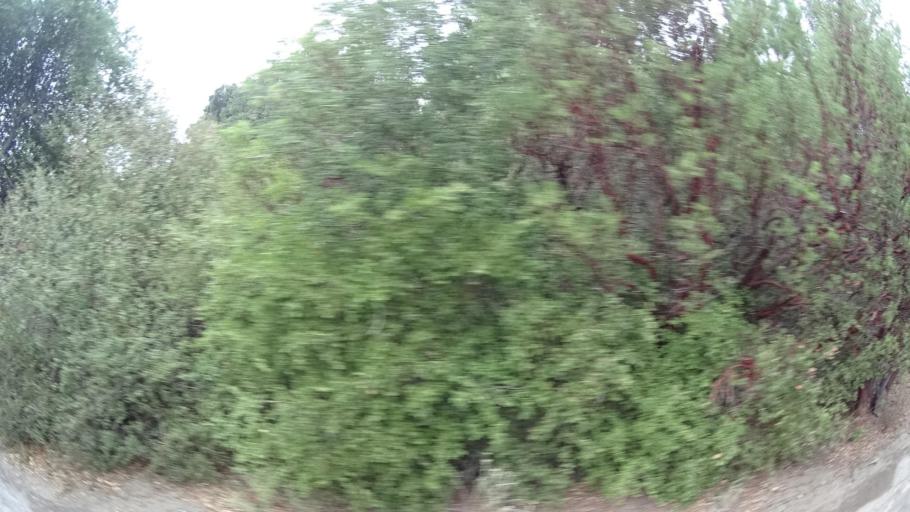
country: US
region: California
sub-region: San Diego County
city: Julian
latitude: 33.0184
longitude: -116.6354
